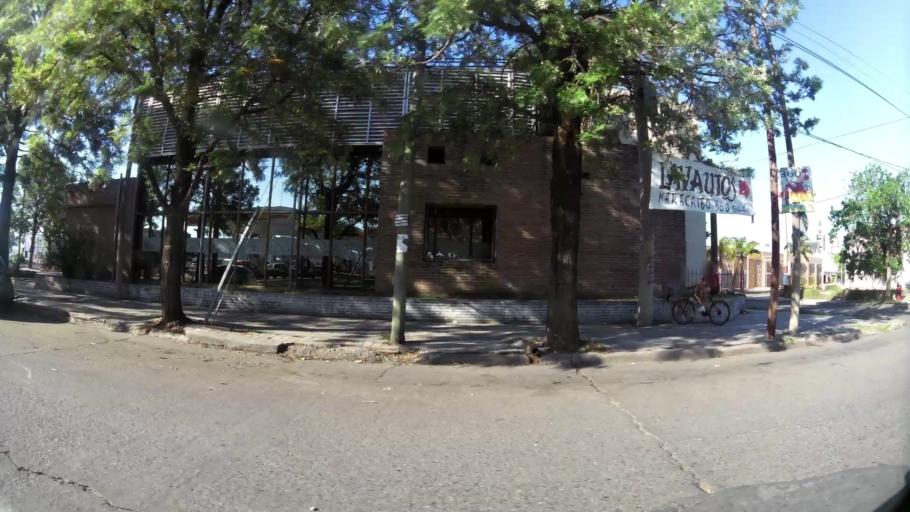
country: AR
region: Cordoba
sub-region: Departamento de Capital
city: Cordoba
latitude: -31.3813
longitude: -64.1755
